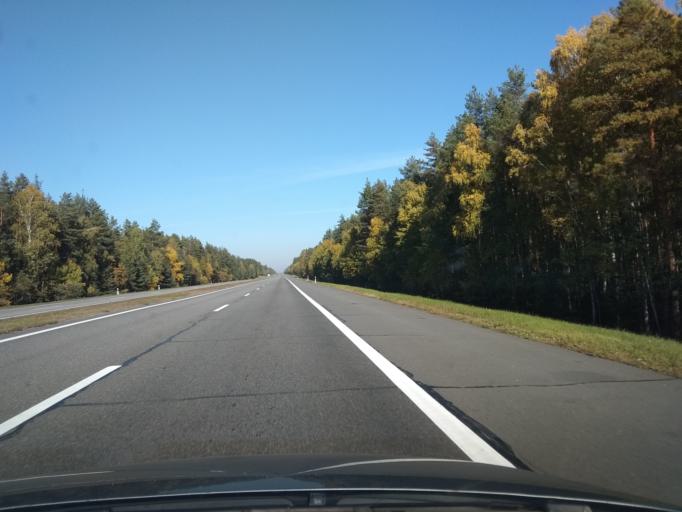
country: BY
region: Grodnenskaya
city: Zhyrovichy
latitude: 52.8679
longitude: 25.6561
